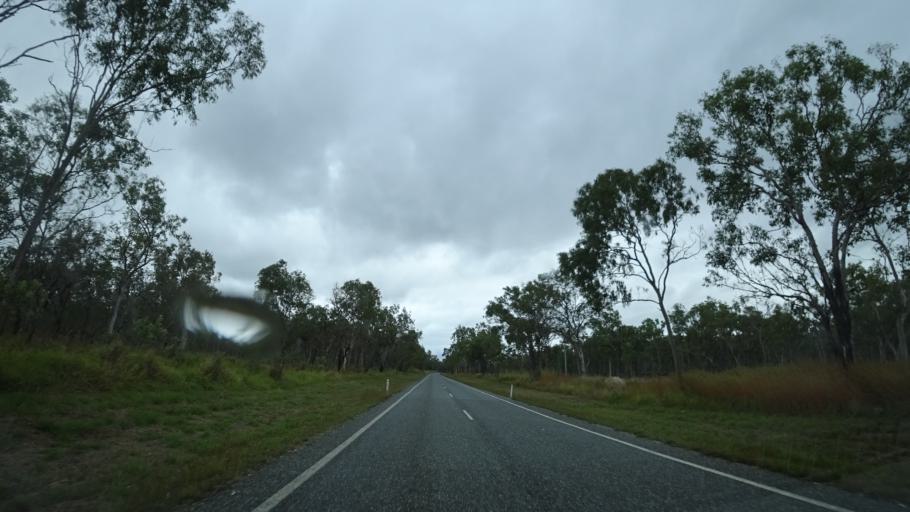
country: AU
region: Queensland
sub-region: Cairns
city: Port Douglas
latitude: -16.7248
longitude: 145.3529
